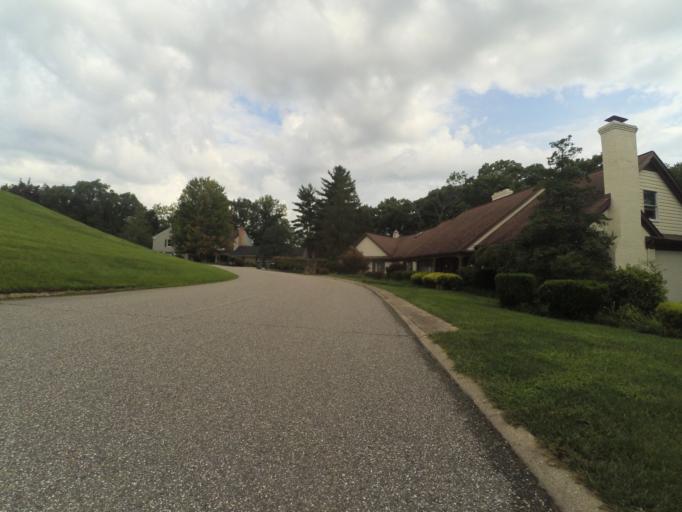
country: US
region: West Virginia
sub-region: Cabell County
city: Huntington
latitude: 38.3999
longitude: -82.4177
